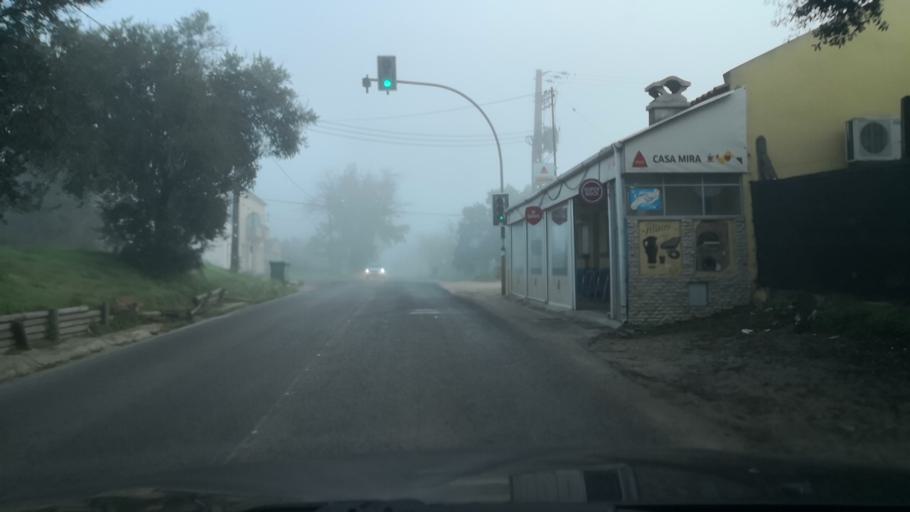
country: PT
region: Setubal
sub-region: Setubal
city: Setubal
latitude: 38.5550
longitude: -8.8416
